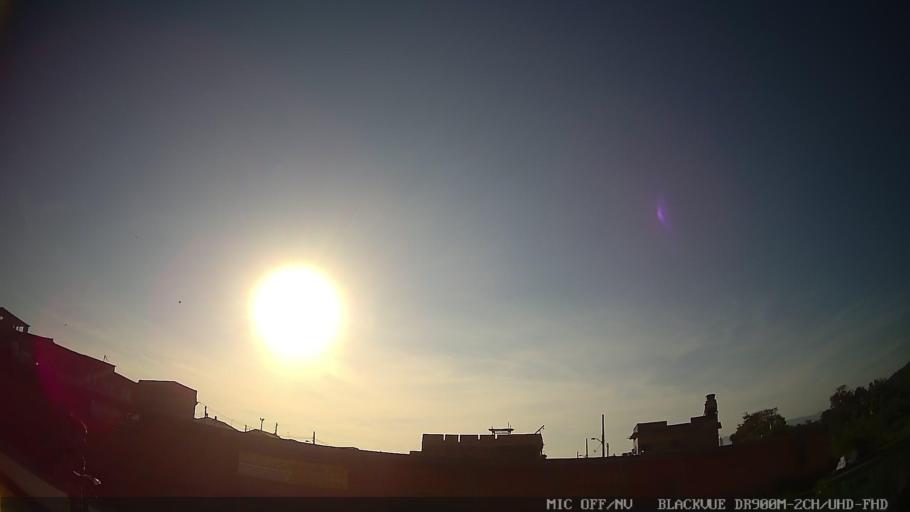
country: BR
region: Sao Paulo
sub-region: Guaruja
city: Guaruja
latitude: -23.9682
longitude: -46.2442
